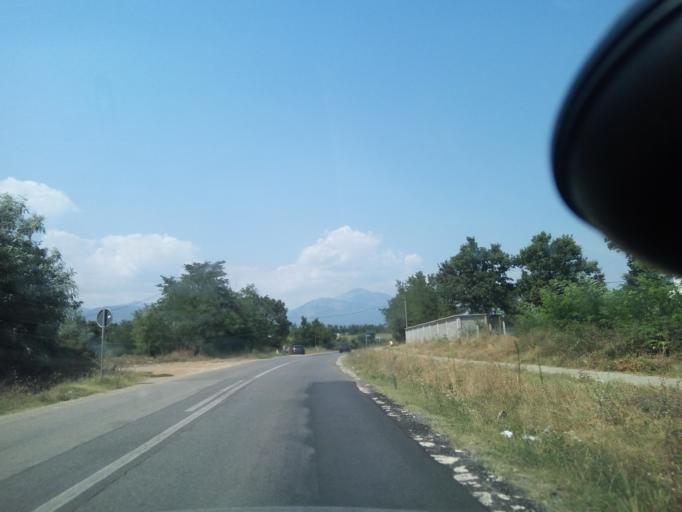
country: XK
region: Gjakova
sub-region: Komuna e Decanit
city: Gllogjan
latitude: 42.4628
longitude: 20.3484
